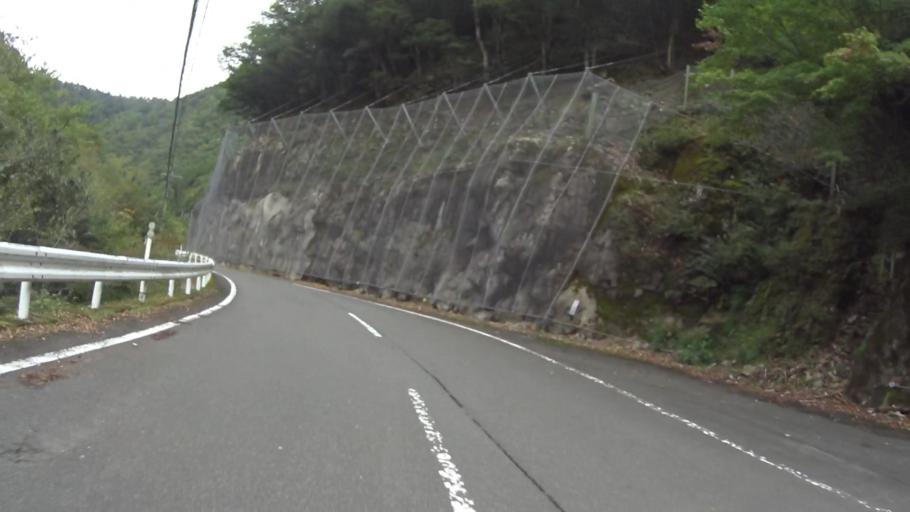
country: JP
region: Fukui
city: Obama
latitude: 35.3072
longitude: 135.6935
